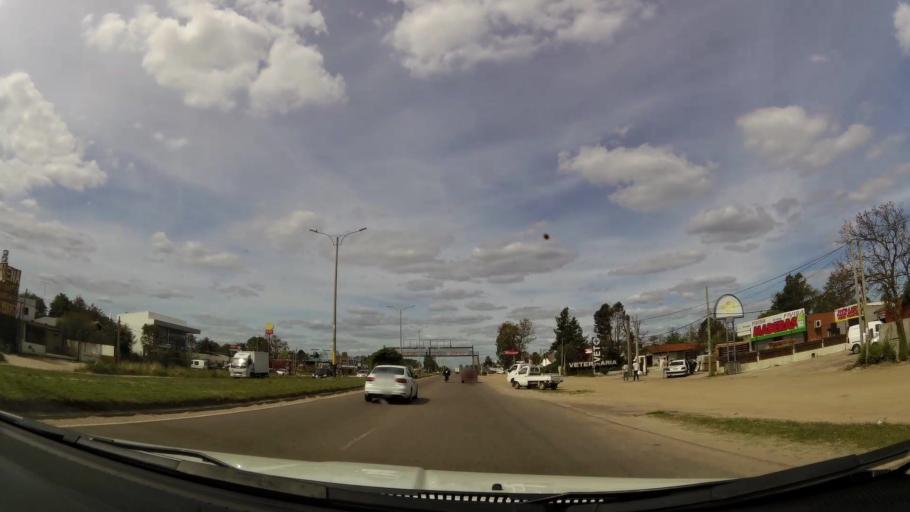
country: UY
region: Canelones
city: Colonia Nicolich
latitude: -34.8266
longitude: -55.9668
